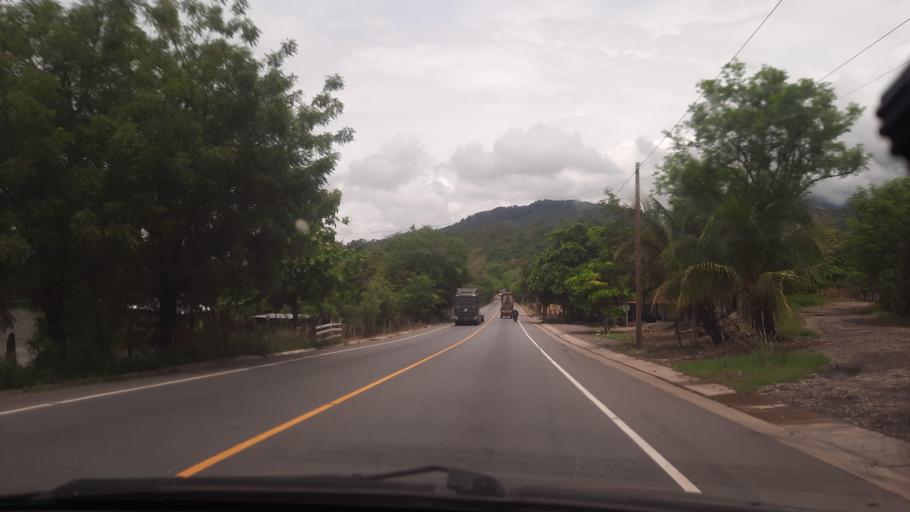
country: GT
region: Izabal
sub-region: Municipio de Los Amates
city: Los Amates
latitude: 15.2164
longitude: -89.2292
